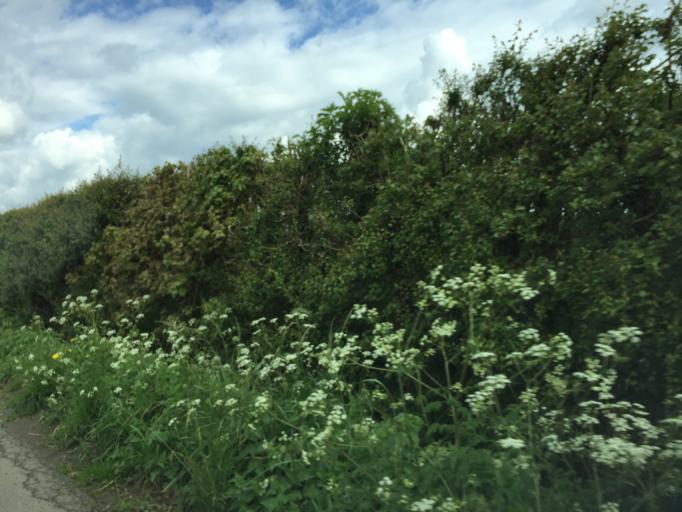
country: GB
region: England
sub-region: Gloucestershire
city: Stonehouse
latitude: 51.7761
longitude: -2.3015
